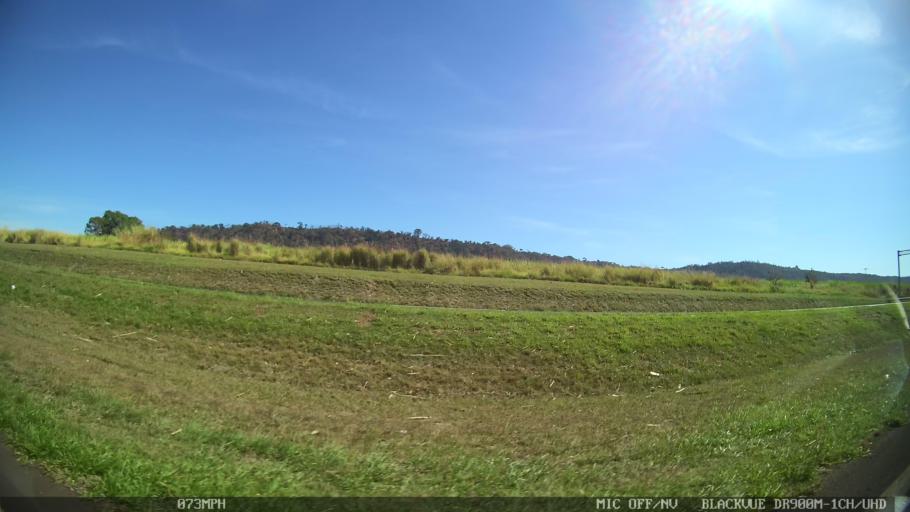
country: BR
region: Sao Paulo
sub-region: Sao Simao
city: Sao Simao
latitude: -21.5155
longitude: -47.6427
